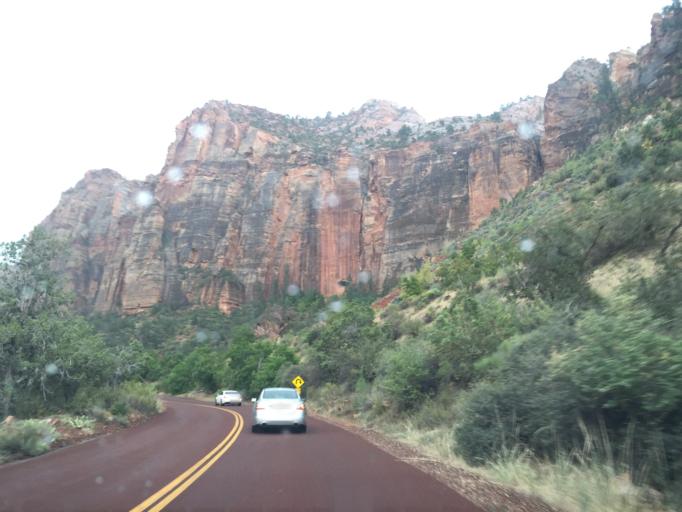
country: US
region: Utah
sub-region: Washington County
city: Hildale
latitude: 37.2128
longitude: -112.9583
